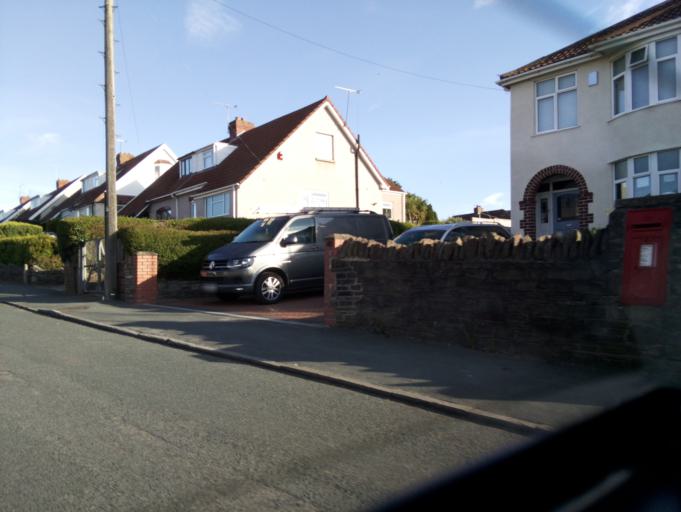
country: GB
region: England
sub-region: South Gloucestershire
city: Mangotsfield
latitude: 51.4883
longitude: -2.4961
